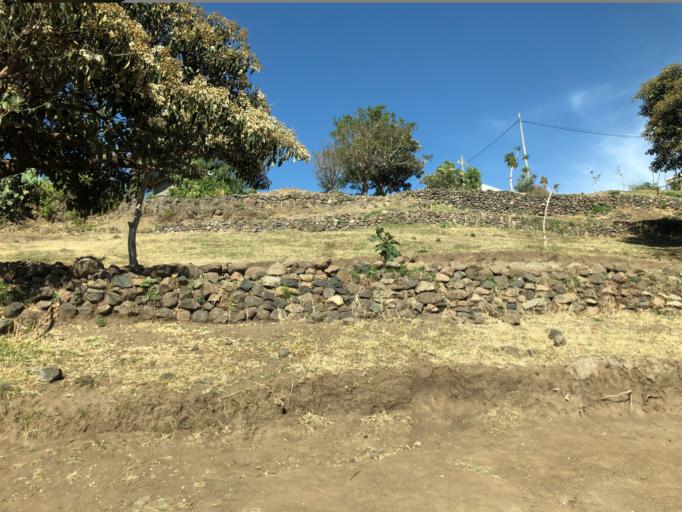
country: ET
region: Amhara
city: Lalibela
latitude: 12.0010
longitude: 39.0645
